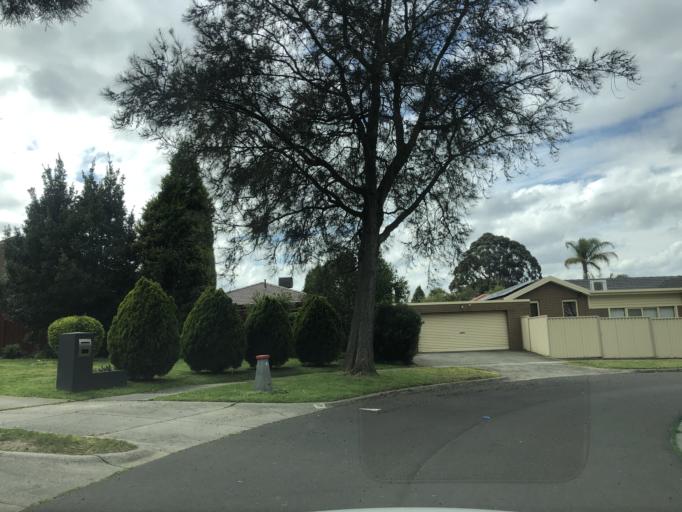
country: AU
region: Victoria
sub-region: Greater Dandenong
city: Noble Park North
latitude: -37.9359
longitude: 145.1946
